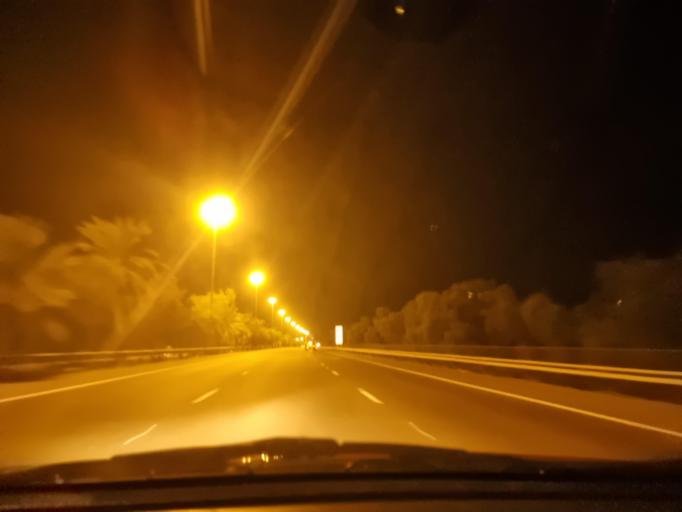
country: AE
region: Abu Dhabi
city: Al Ain
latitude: 24.1750
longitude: 55.2031
